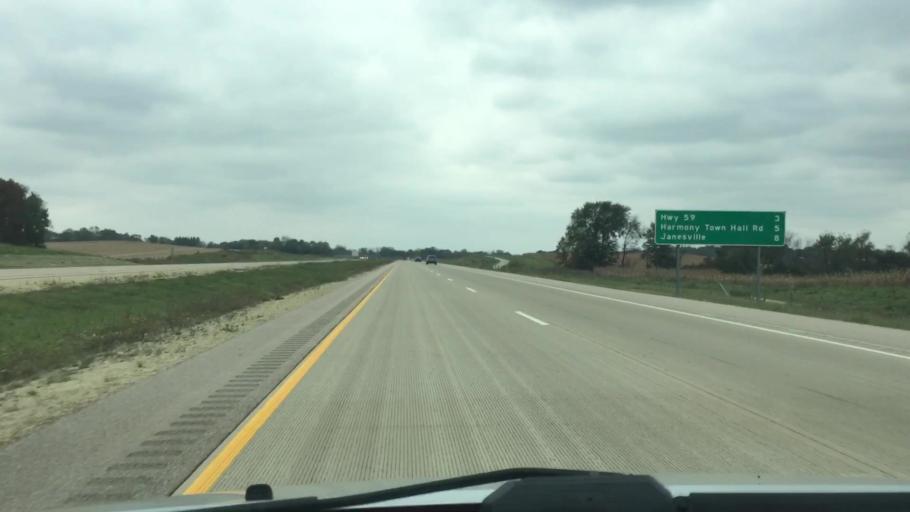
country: US
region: Wisconsin
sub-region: Rock County
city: Milton
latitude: 42.8109
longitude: -88.9272
